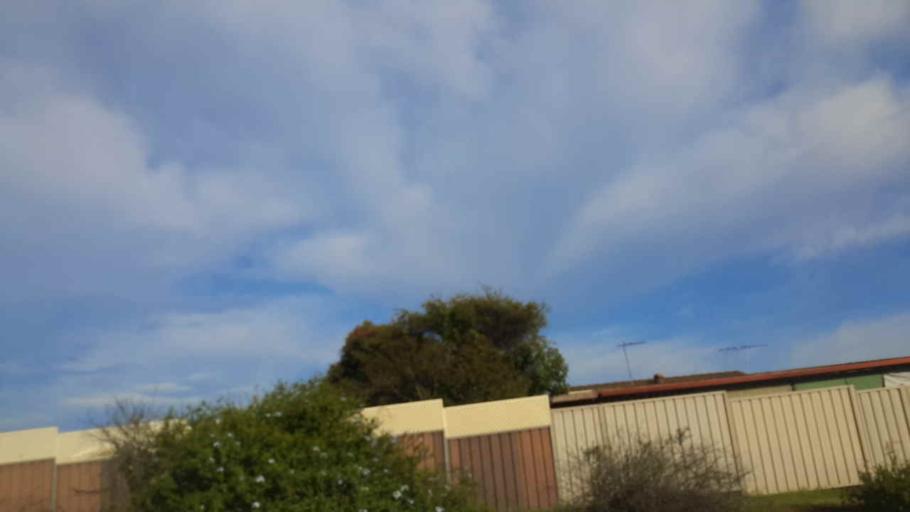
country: AU
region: New South Wales
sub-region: Campbelltown Municipality
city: Glen Alpine
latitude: -34.1028
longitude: 150.8017
